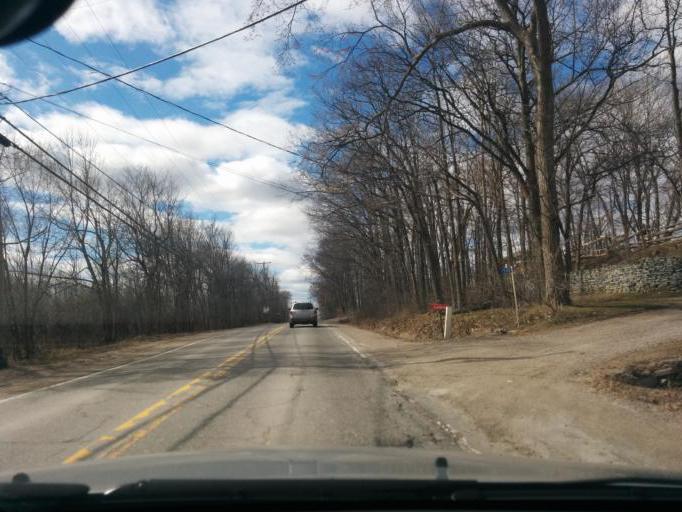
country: CA
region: Ontario
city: Bells Corners
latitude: 45.4394
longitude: -75.9140
